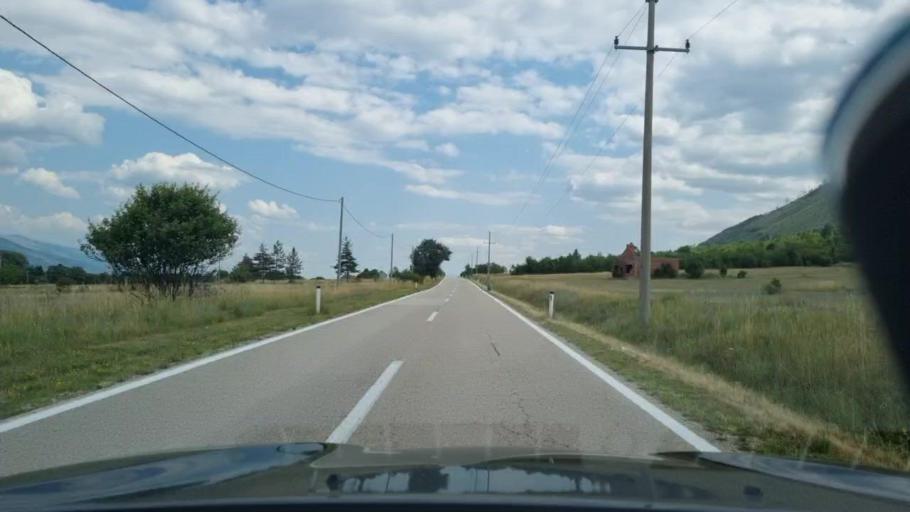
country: BA
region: Federation of Bosnia and Herzegovina
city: Bosansko Grahovo
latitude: 44.0658
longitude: 16.5794
